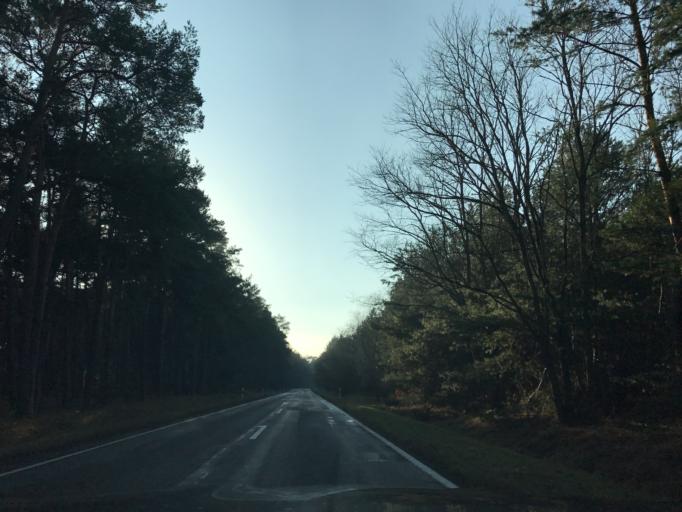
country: DE
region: Brandenburg
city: Wenzlow
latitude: 52.2838
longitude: 12.4442
